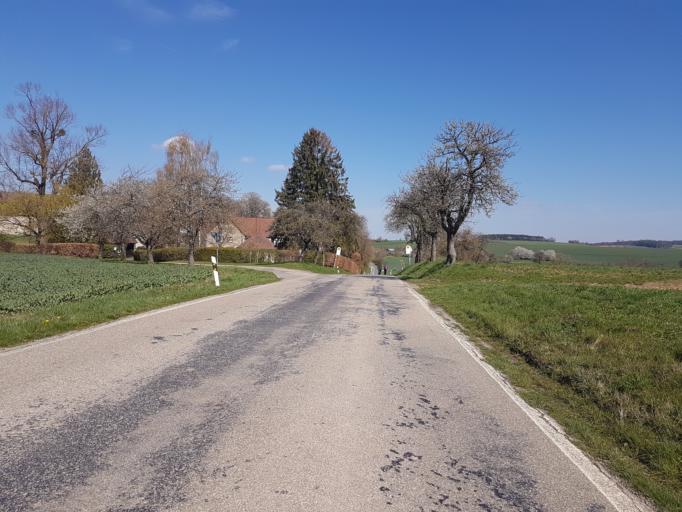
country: DE
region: Baden-Wuerttemberg
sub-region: Regierungsbezirk Stuttgart
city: Jagsthausen
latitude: 49.3455
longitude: 9.4844
